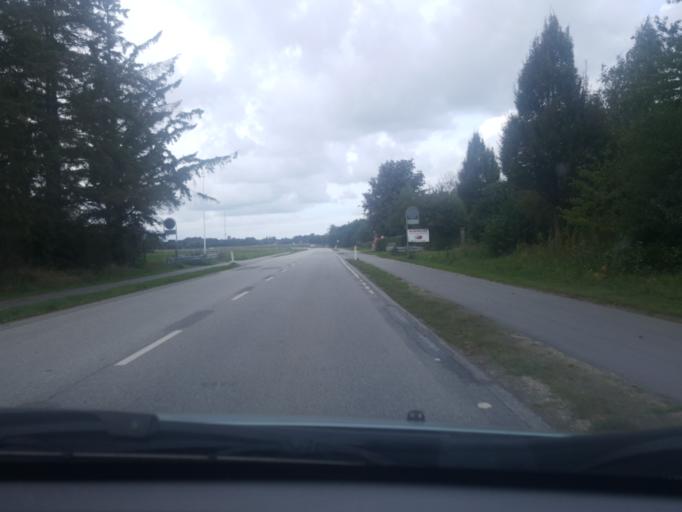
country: DK
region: Zealand
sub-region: Guldborgsund Kommune
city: Nykobing Falster
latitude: 54.6982
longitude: 11.9481
